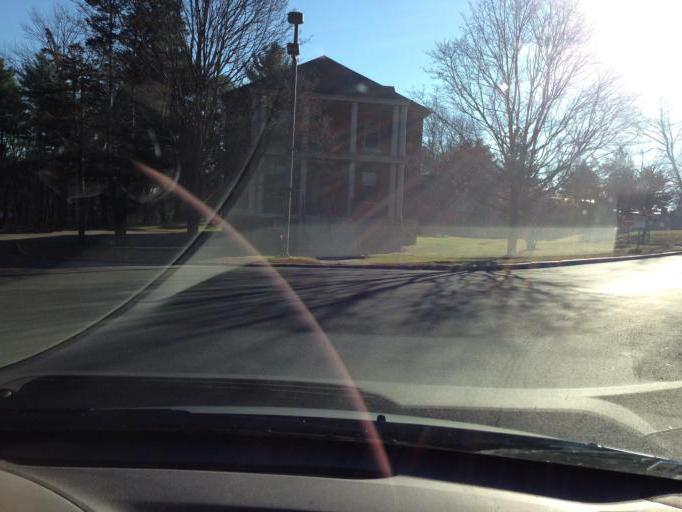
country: US
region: Massachusetts
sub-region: Middlesex County
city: Bedford
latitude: 42.5072
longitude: -71.2736
